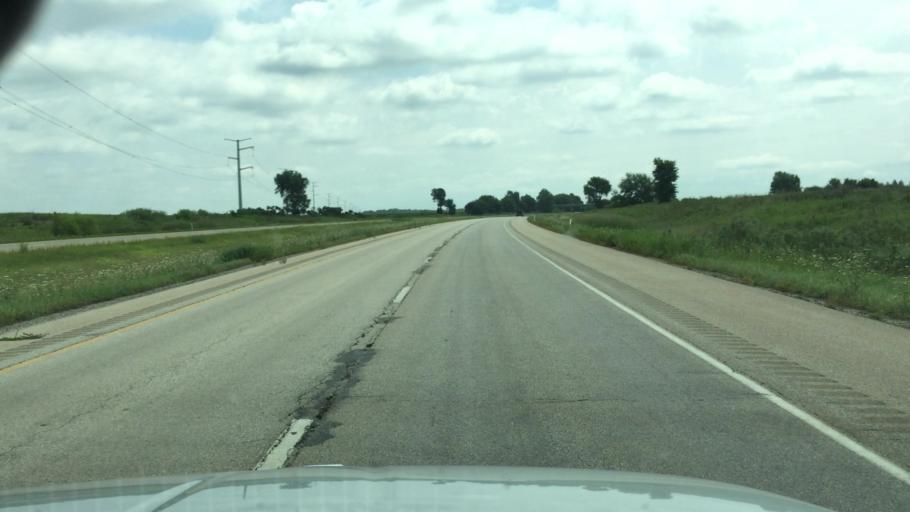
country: US
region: Illinois
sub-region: Knox County
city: Knoxville
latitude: 40.9023
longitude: -90.1660
